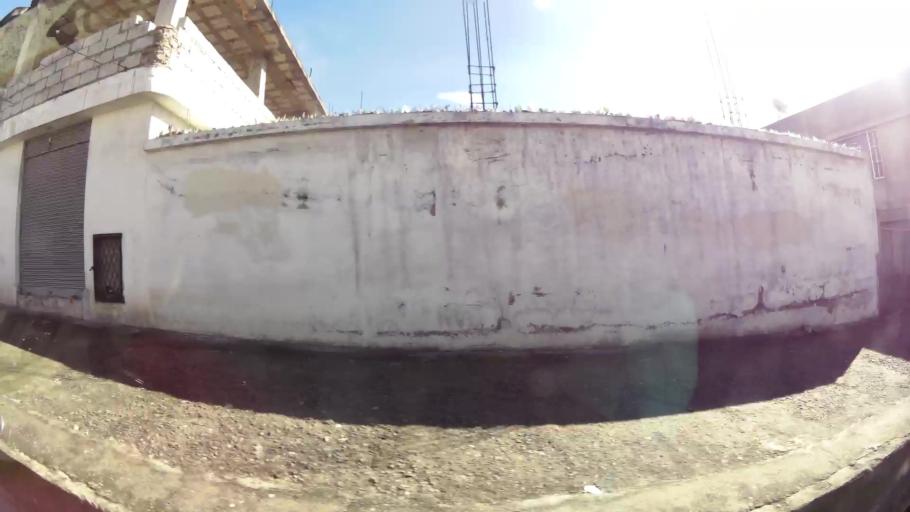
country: EC
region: Pichincha
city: Quito
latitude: -0.3041
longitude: -78.5633
